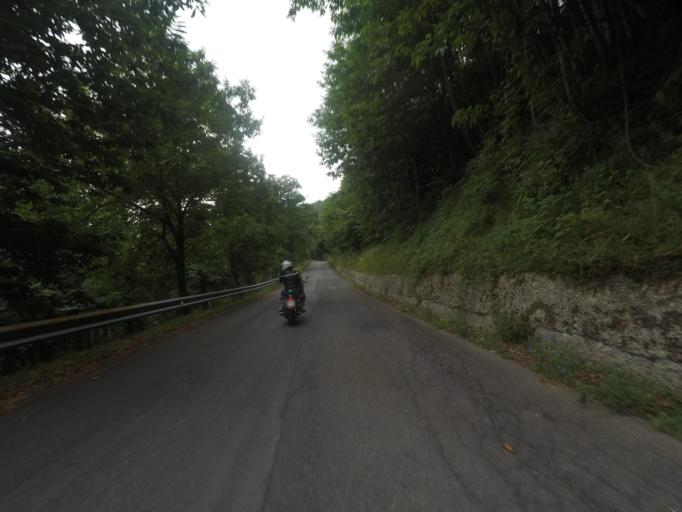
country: IT
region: Tuscany
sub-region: Provincia di Lucca
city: Careggine
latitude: 44.1163
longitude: 10.3613
